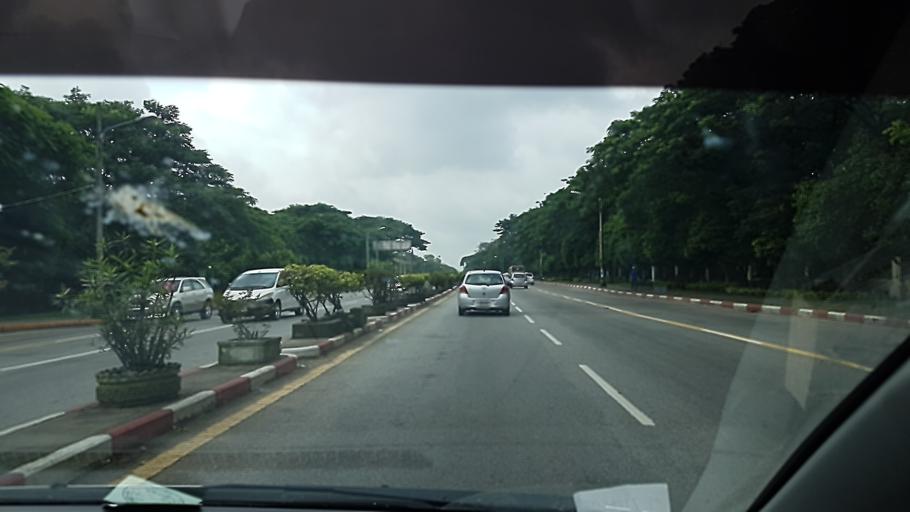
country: MM
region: Yangon
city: Yangon
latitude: 16.7982
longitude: 96.1388
